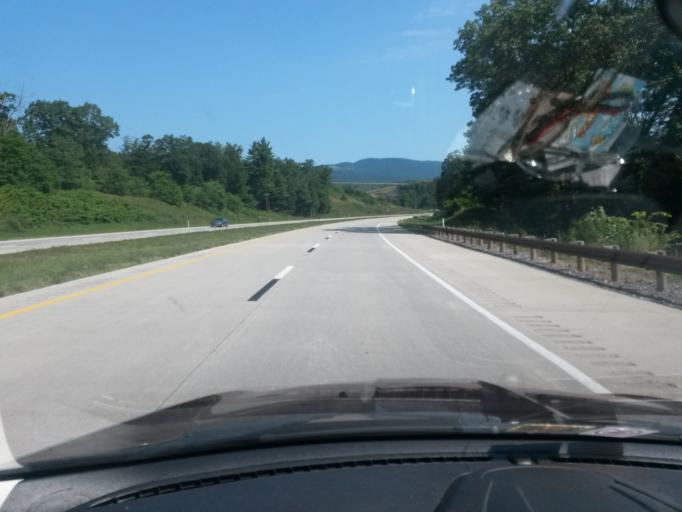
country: US
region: West Virginia
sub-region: Hardy County
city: Moorefield
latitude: 39.1276
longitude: -78.9829
